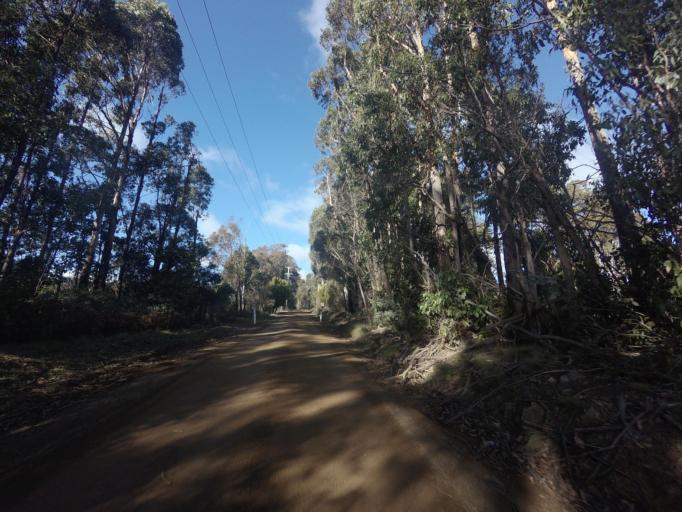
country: AU
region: Tasmania
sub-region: Derwent Valley
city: New Norfolk
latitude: -42.8356
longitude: 147.1319
